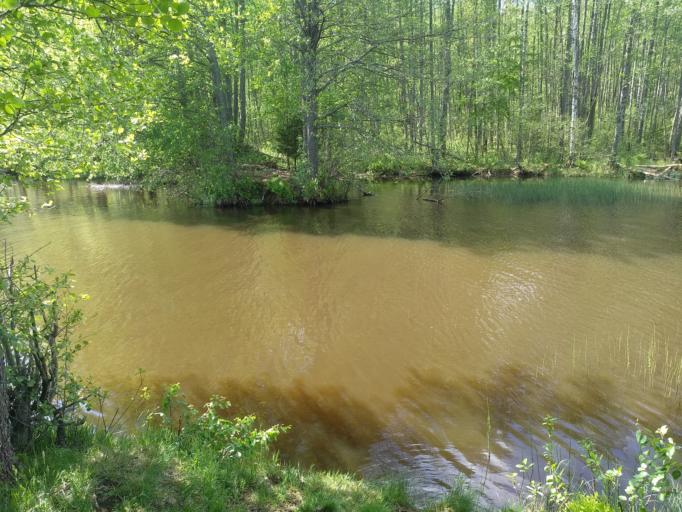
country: RU
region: Leningrad
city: Michurinskoye
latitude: 60.6010
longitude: 29.8646
